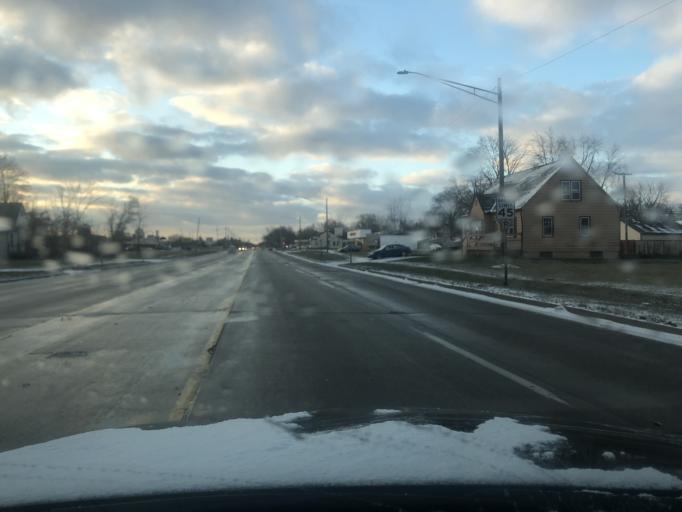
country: US
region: Michigan
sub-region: Wayne County
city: Garden City
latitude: 42.2998
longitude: -83.3493
